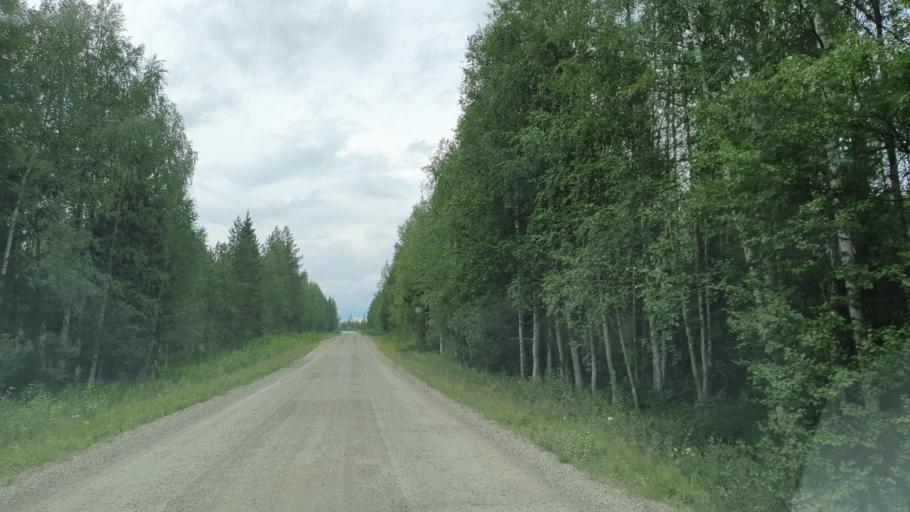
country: FI
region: Kainuu
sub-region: Kehys-Kainuu
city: Kuhmo
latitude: 64.7238
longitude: 29.6758
